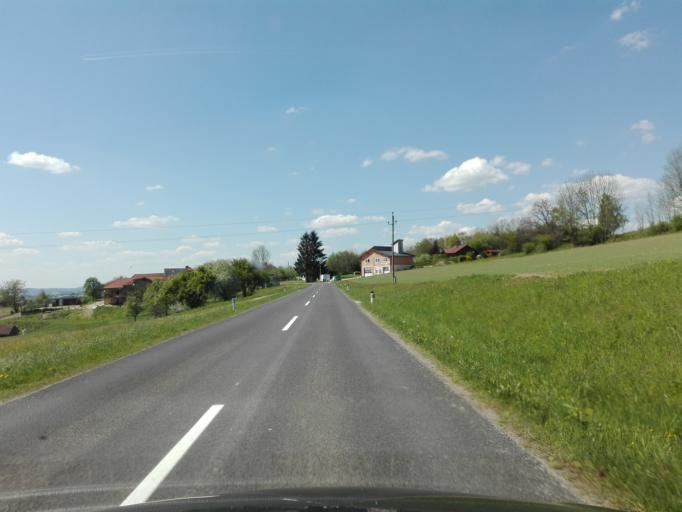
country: AT
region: Upper Austria
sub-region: Politischer Bezirk Rohrbach
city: Kleinzell im Muehlkreis
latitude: 48.3657
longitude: 13.9279
